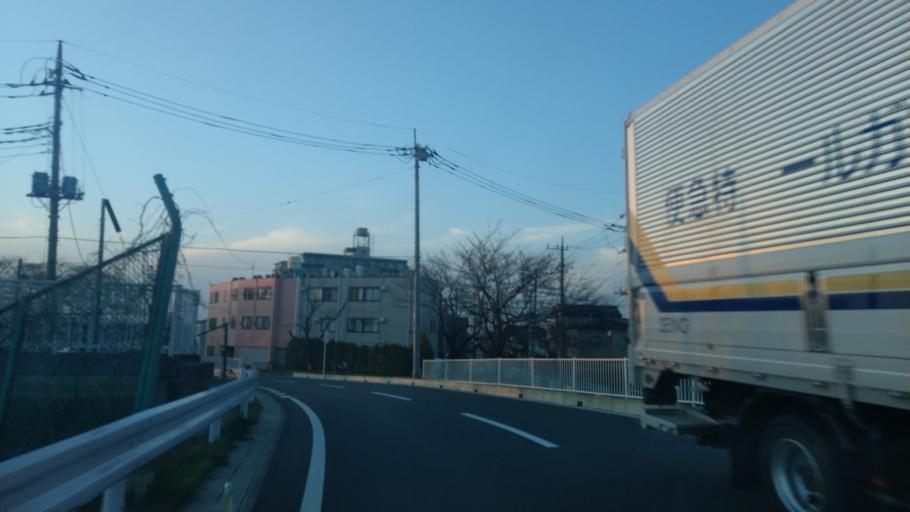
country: JP
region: Saitama
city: Yono
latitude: 35.8526
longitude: 139.6158
